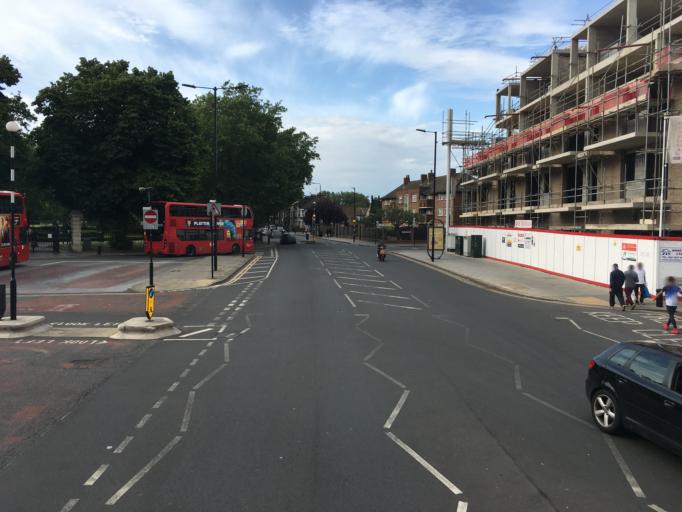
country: GB
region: England
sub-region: Greater London
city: East Ham
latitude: 51.5277
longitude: 0.0563
